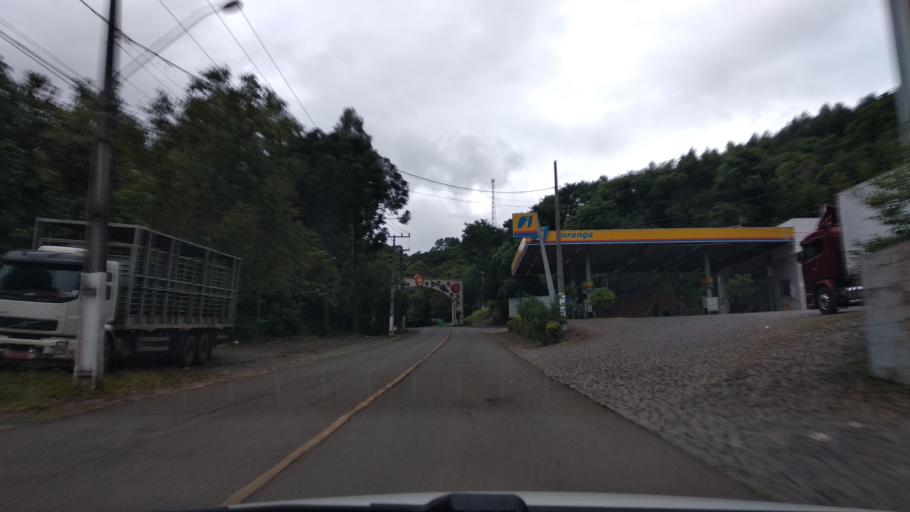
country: BR
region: Santa Catarina
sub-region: Videira
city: Videira
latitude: -27.0469
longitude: -51.2216
